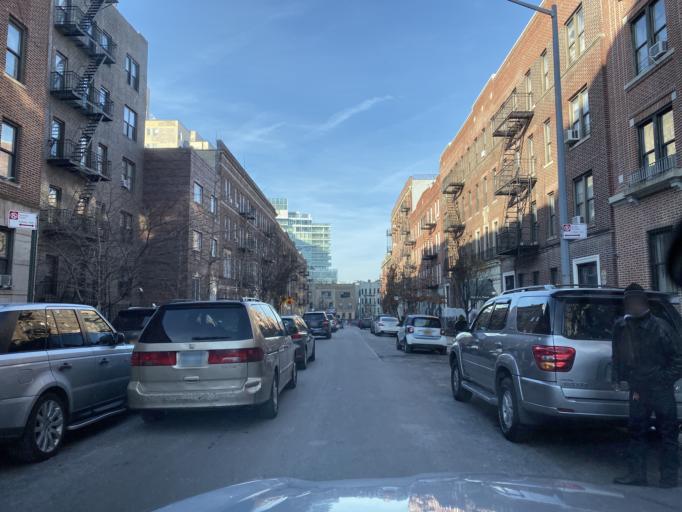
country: US
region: New York
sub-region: Kings County
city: Brooklyn
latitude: 40.6733
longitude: -73.9655
